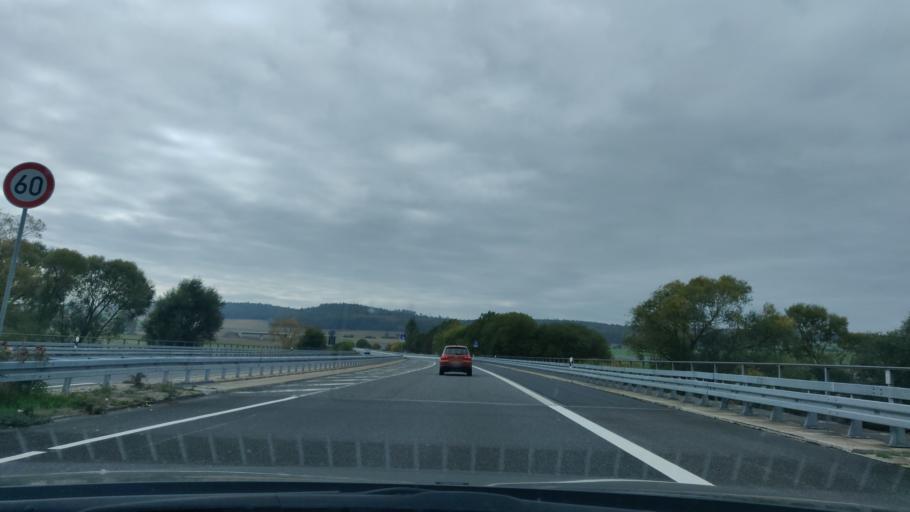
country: DE
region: Hesse
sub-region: Regierungsbezirk Kassel
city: Neuental
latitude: 51.0078
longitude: 9.2065
